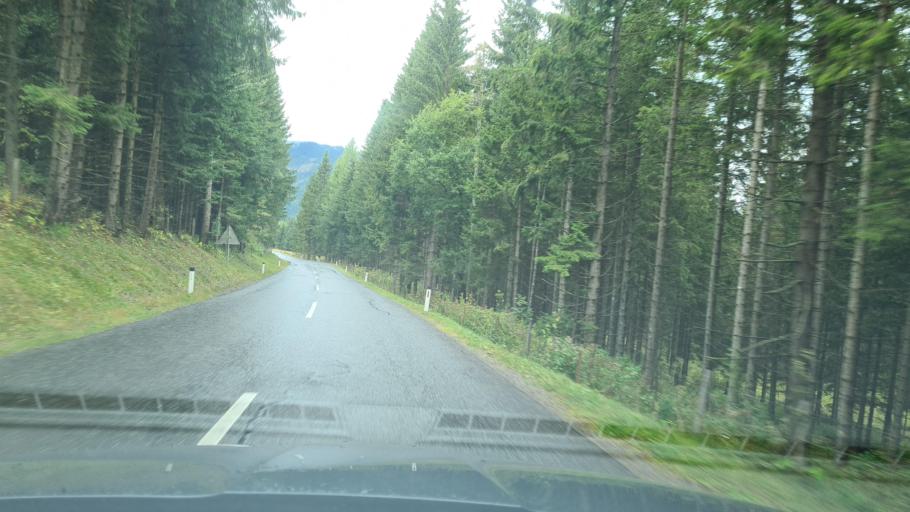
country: AT
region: Styria
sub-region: Politischer Bezirk Weiz
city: Passail
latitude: 47.3439
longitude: 15.4761
